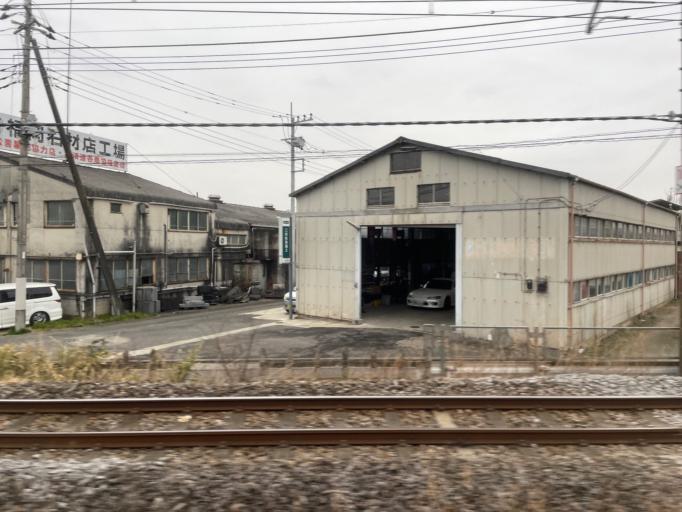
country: JP
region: Gunma
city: Maebashi-shi
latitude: 36.4050
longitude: 139.0384
